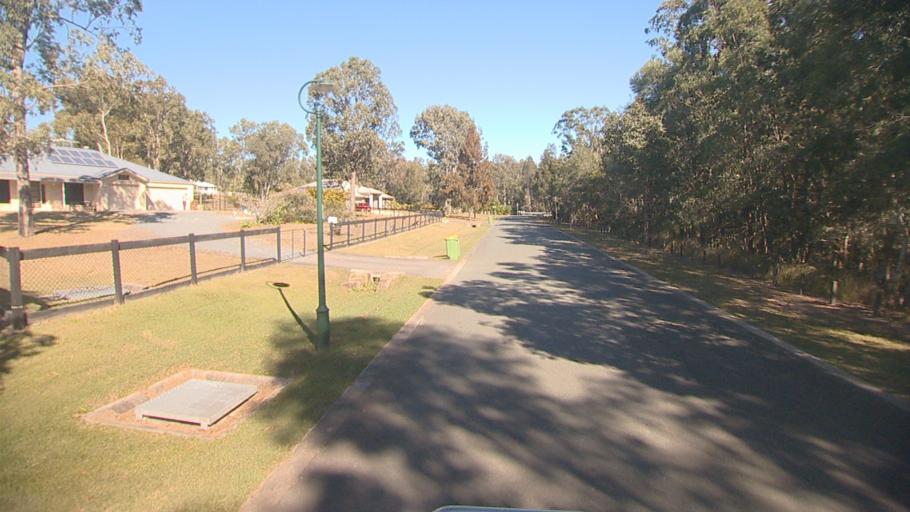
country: AU
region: Queensland
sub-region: Logan
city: North Maclean
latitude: -27.7574
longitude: 152.9612
